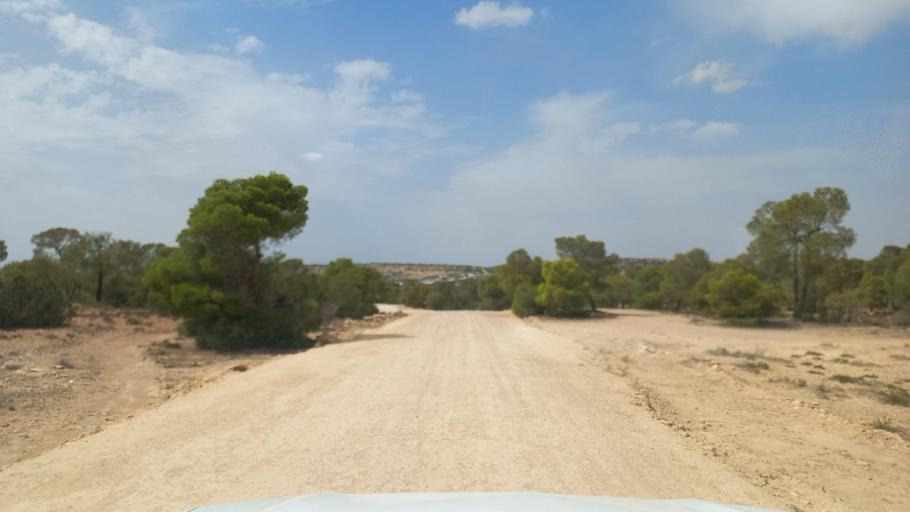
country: TN
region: Al Qasrayn
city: Kasserine
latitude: 35.3825
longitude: 8.8756
